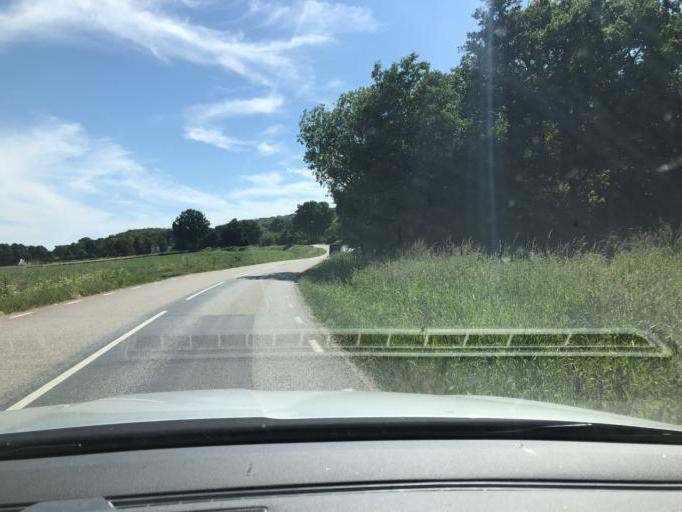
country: SE
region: Blekinge
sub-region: Solvesborgs Kommun
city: Soelvesborg
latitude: 56.0902
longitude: 14.6077
